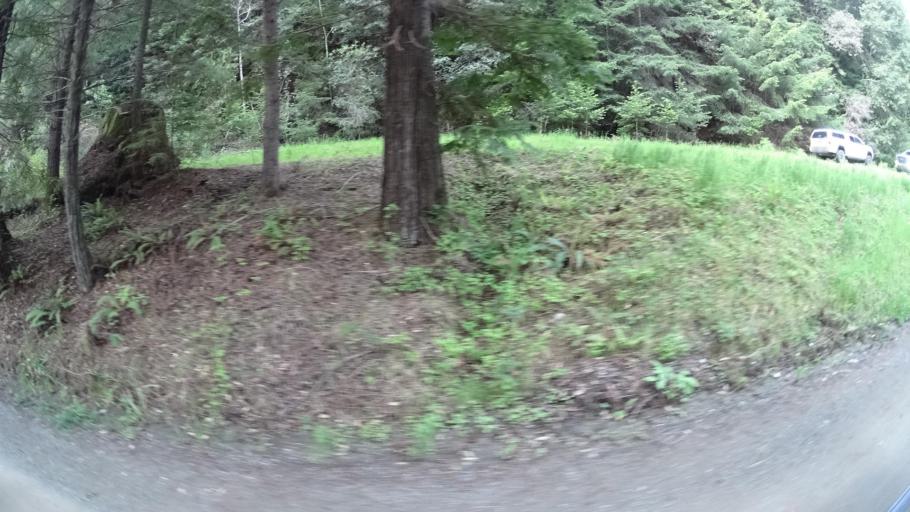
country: US
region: California
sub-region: Humboldt County
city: Redway
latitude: 40.3278
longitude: -123.8421
